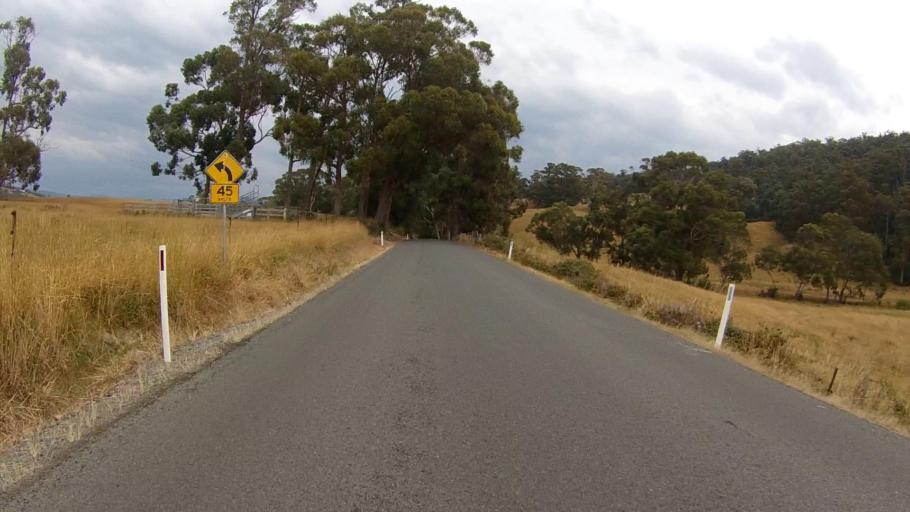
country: AU
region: Tasmania
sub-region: Huon Valley
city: Cygnet
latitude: -43.1804
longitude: 147.1169
